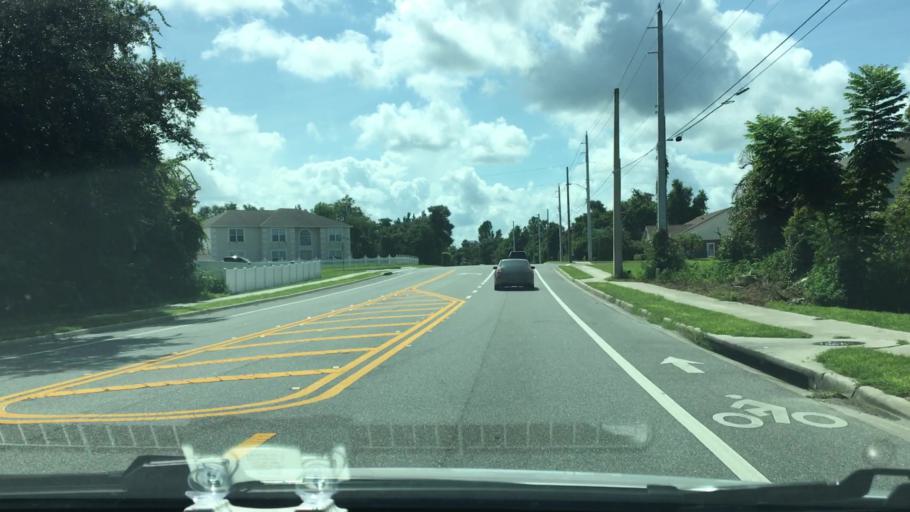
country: US
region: Florida
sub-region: Volusia County
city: Deltona
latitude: 28.8795
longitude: -81.2046
